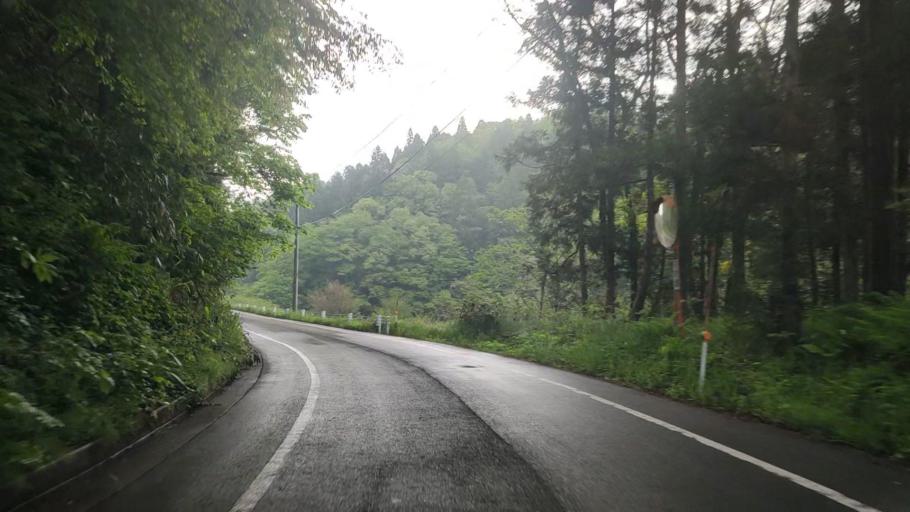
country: JP
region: Niigata
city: Gosen
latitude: 37.7135
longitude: 139.1224
